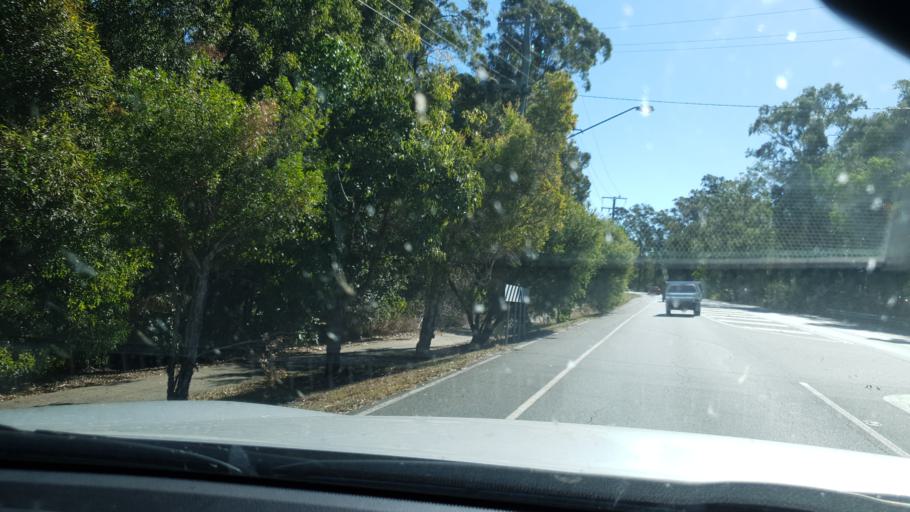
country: AU
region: Queensland
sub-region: Moreton Bay
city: Strathpine
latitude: -27.3315
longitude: 152.9529
